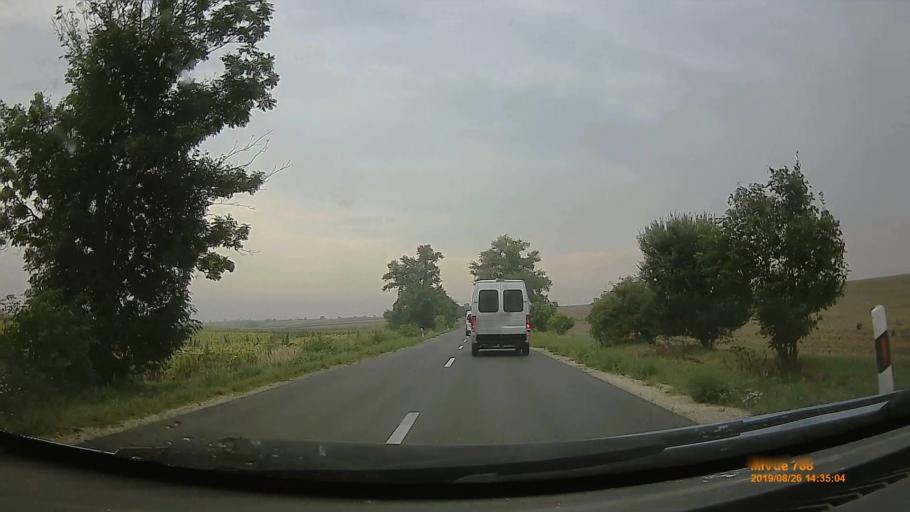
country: HU
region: Fejer
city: Szekesfehervar
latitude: 47.2520
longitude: 18.4191
